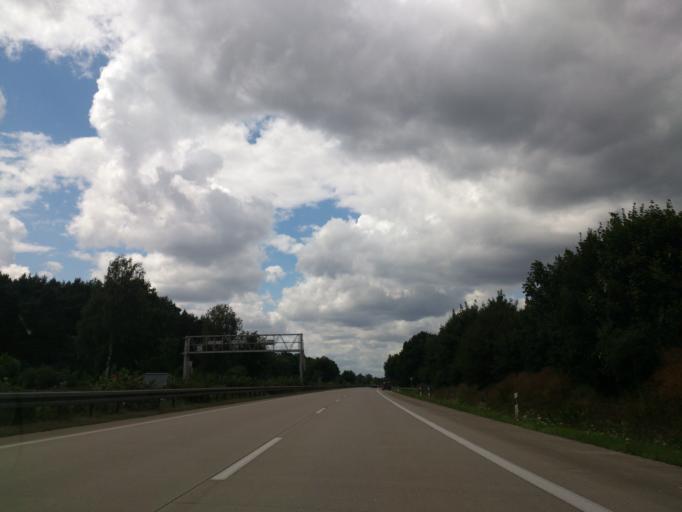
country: DE
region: Lower Saxony
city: Langenhagen
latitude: 52.5058
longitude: 9.7598
